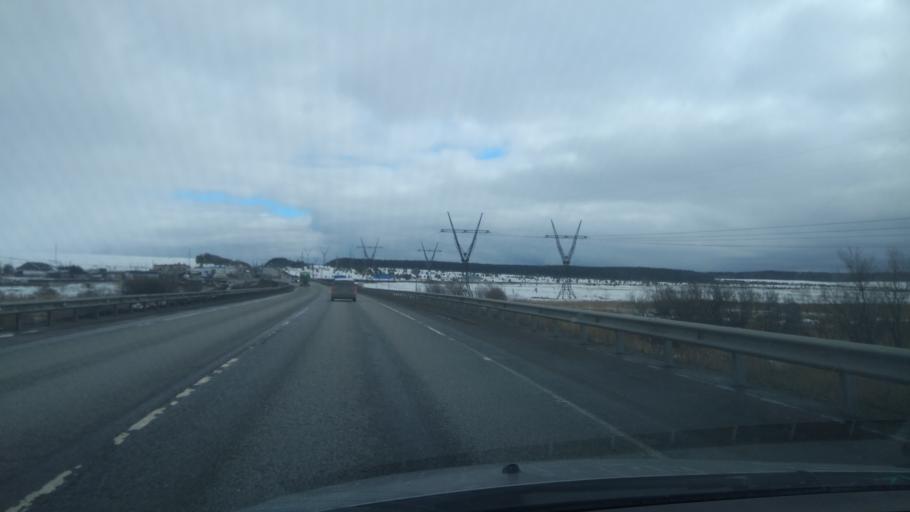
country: RU
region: Sverdlovsk
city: Achit
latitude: 56.7833
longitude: 57.9000
